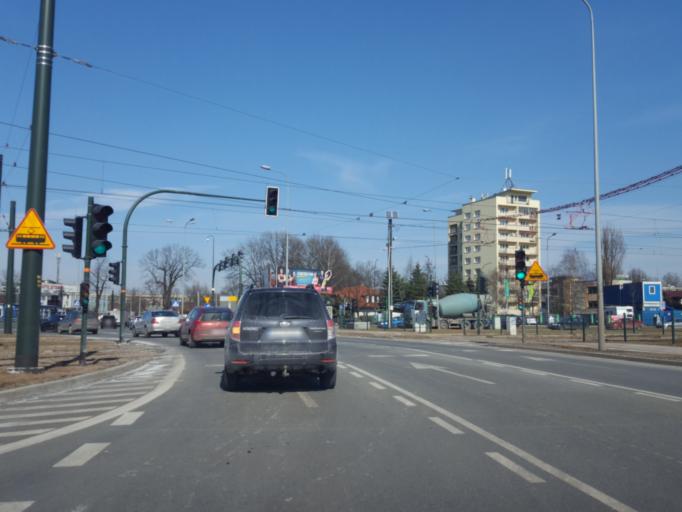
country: PL
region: Lesser Poland Voivodeship
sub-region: Krakow
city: Krakow
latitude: 50.0732
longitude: 20.0177
